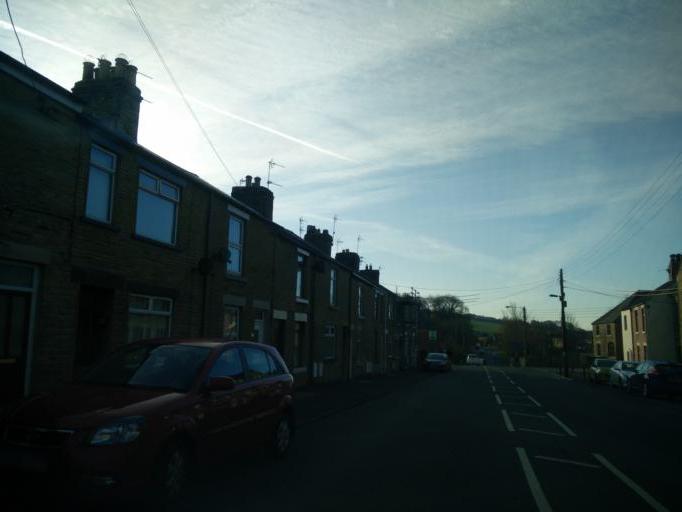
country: GB
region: England
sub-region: County Durham
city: Crook
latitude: 54.6948
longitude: -1.7485
